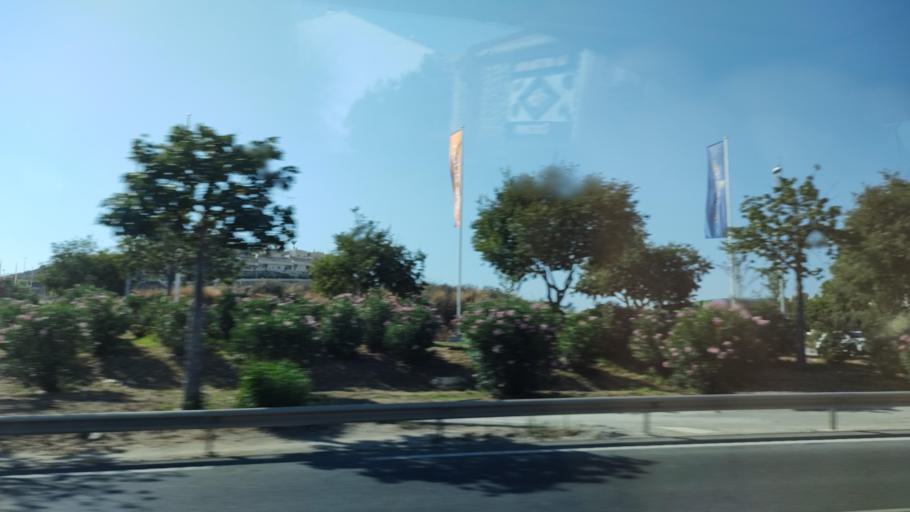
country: ES
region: Andalusia
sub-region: Provincia de Malaga
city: Fuengirola
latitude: 36.5018
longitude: -4.6850
